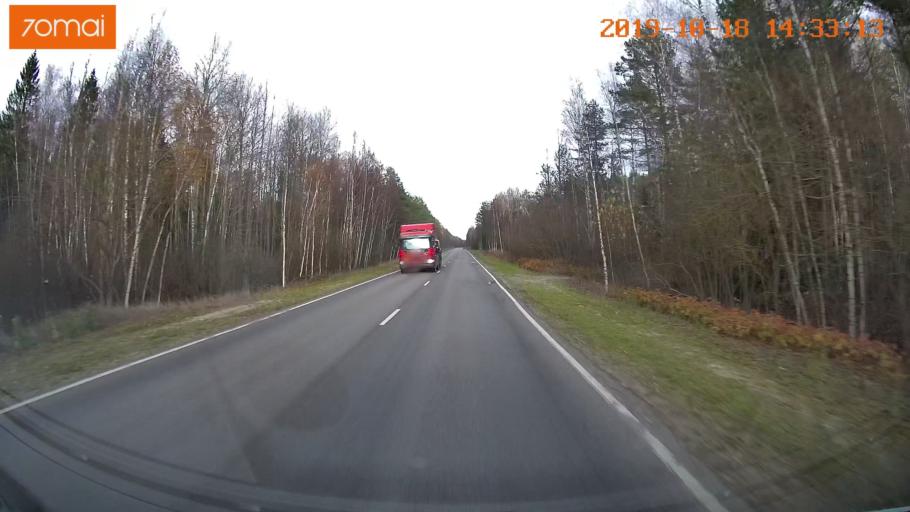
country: RU
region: Rjazan
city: Tuma
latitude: 55.1989
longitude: 40.5926
